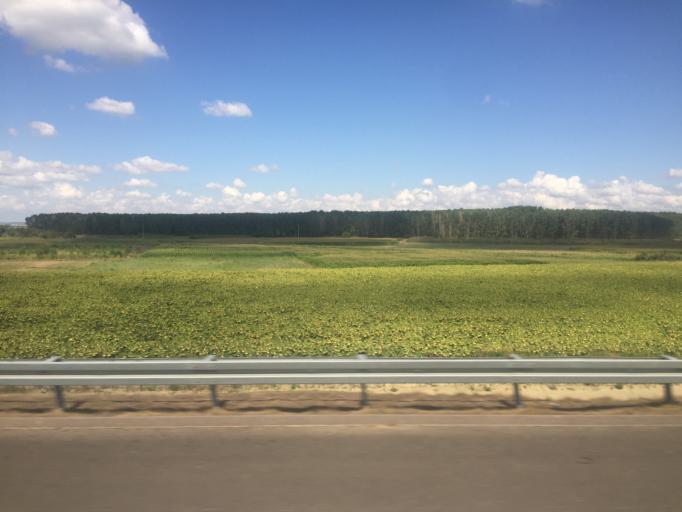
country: TR
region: Bursa
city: Karacabey
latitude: 40.1426
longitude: 28.3036
